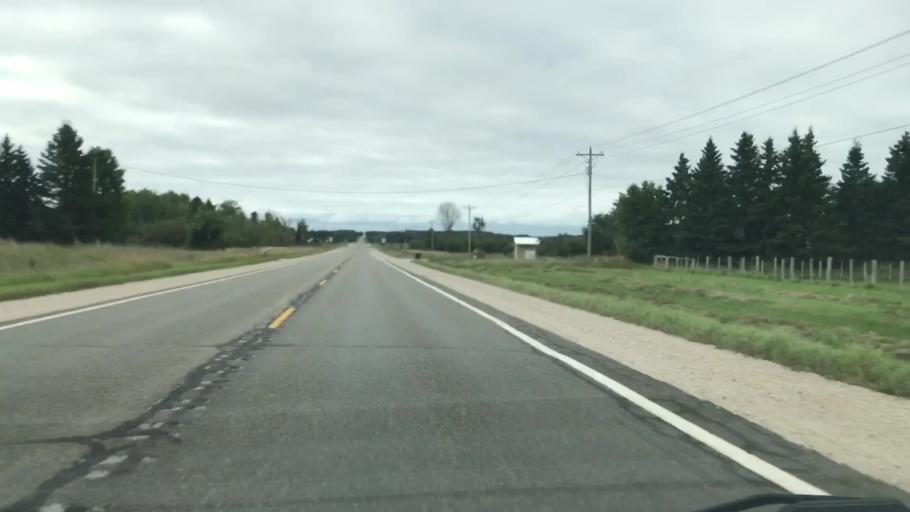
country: US
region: Michigan
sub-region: Luce County
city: Newberry
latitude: 46.1512
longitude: -85.5714
